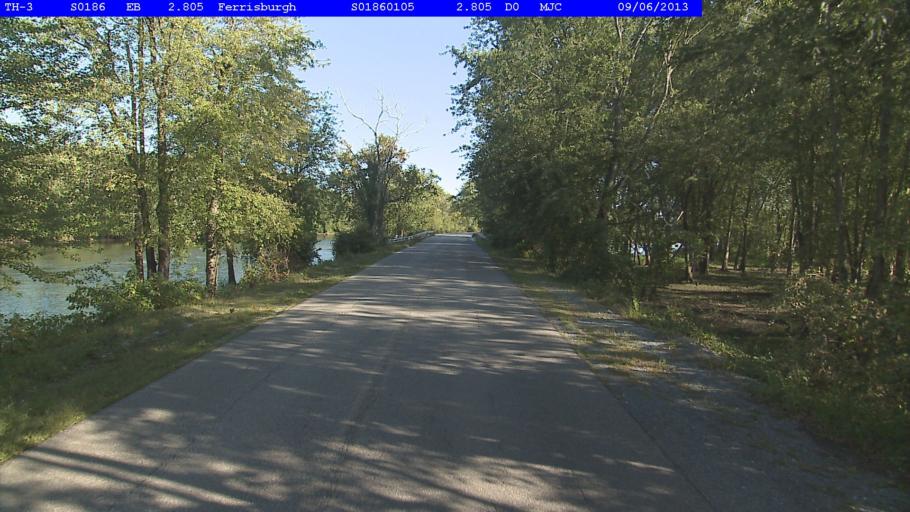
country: US
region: Vermont
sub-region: Addison County
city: Vergennes
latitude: 44.1857
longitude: -73.3116
